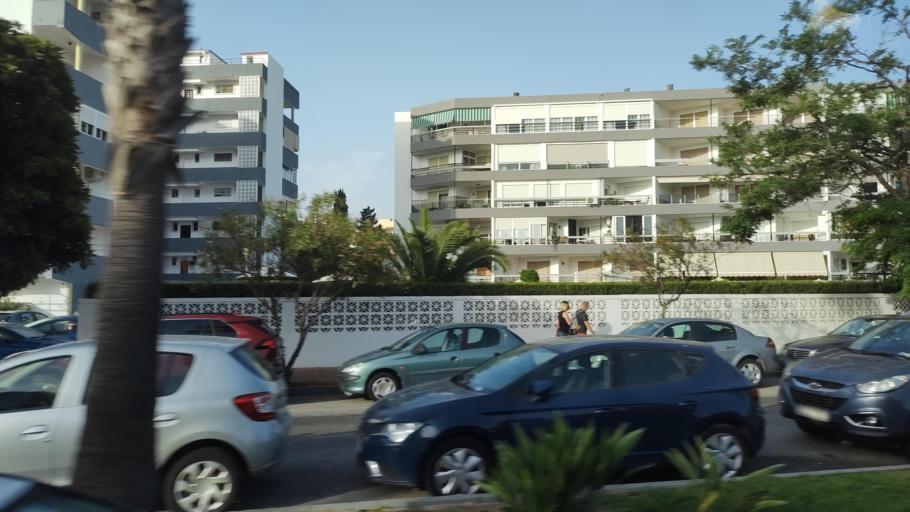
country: ES
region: Andalusia
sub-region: Provincia de Malaga
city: Torremolinos
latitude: 36.6430
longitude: -4.4820
